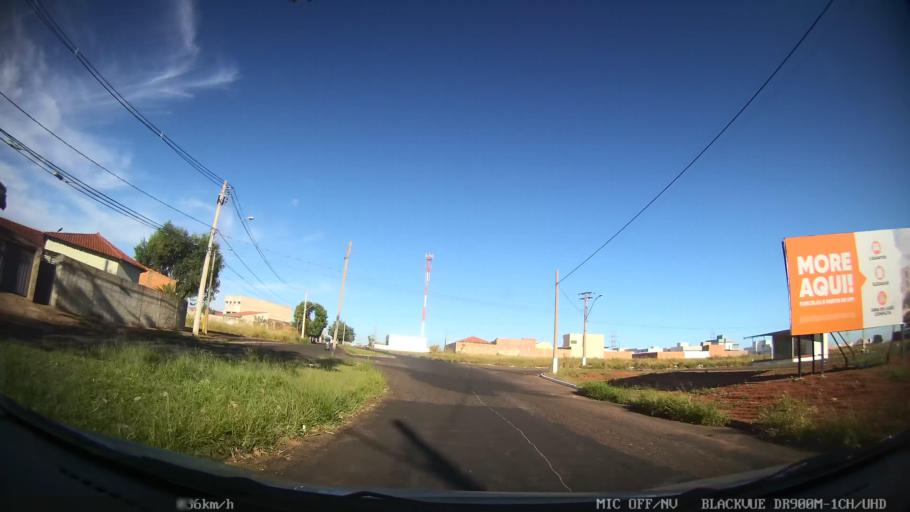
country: BR
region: Sao Paulo
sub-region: Americo Brasiliense
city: Americo Brasiliense
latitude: -21.7442
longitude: -48.1511
